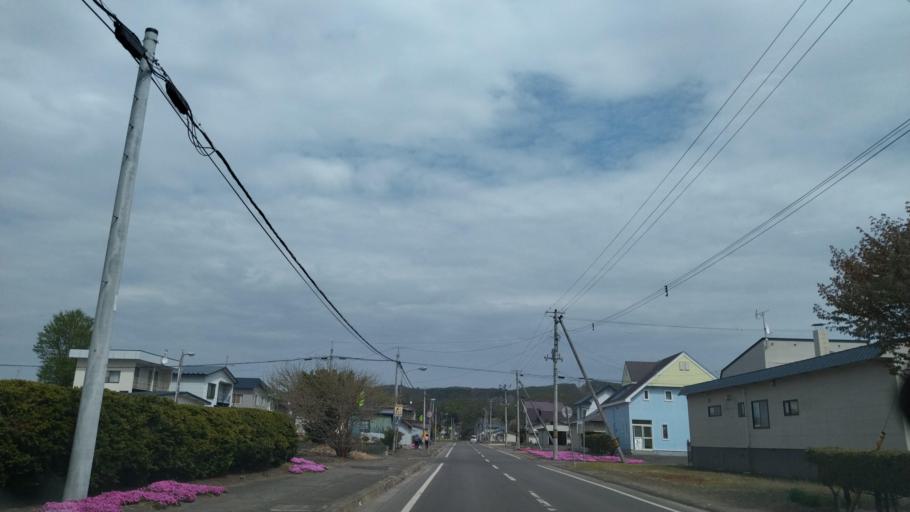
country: JP
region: Hokkaido
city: Otofuke
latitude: 43.2367
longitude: 143.5535
